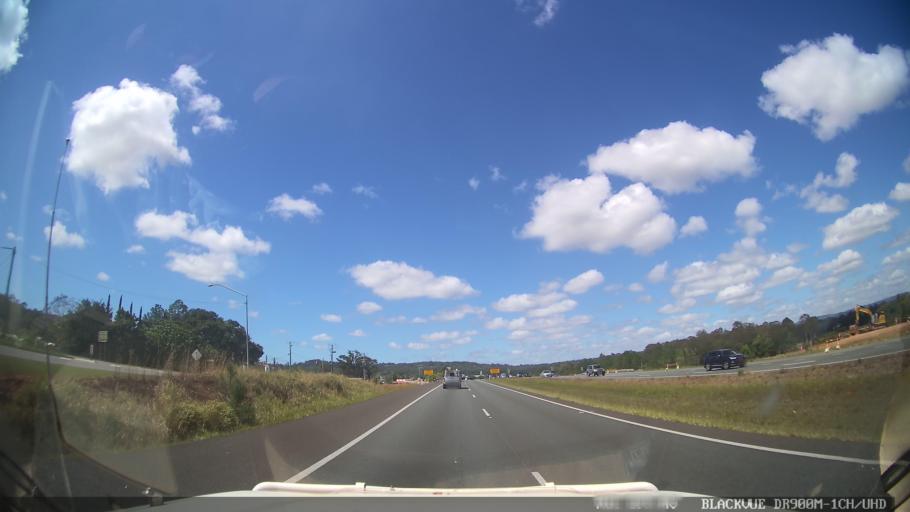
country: AU
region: Queensland
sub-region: Sunshine Coast
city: Woombye
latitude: -26.6841
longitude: 153.0033
